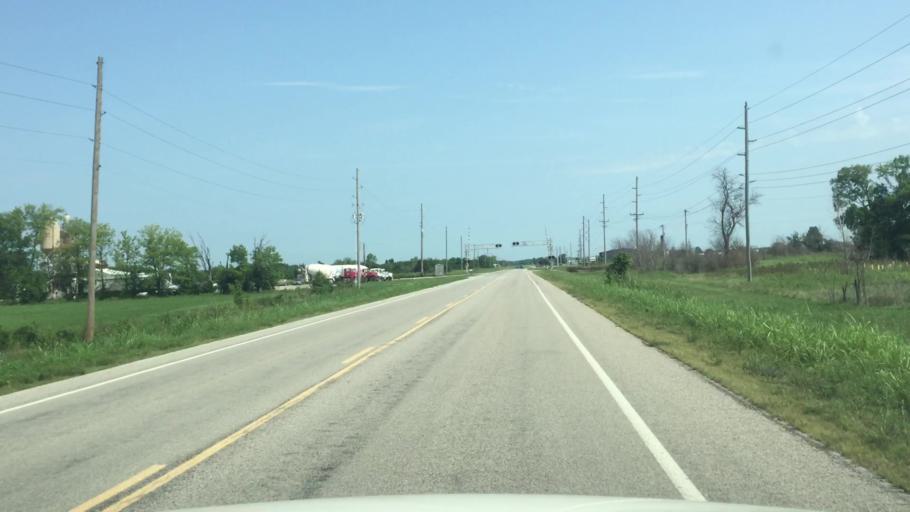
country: US
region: Kansas
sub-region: Montgomery County
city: Coffeyville
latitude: 37.0849
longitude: -95.5863
